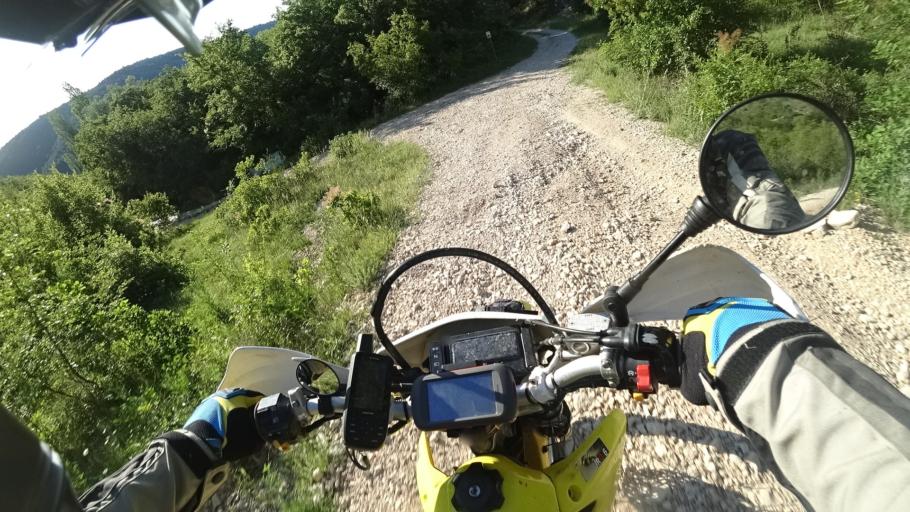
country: HR
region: Sibensko-Kniniska
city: Drnis
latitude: 43.8188
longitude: 16.0203
